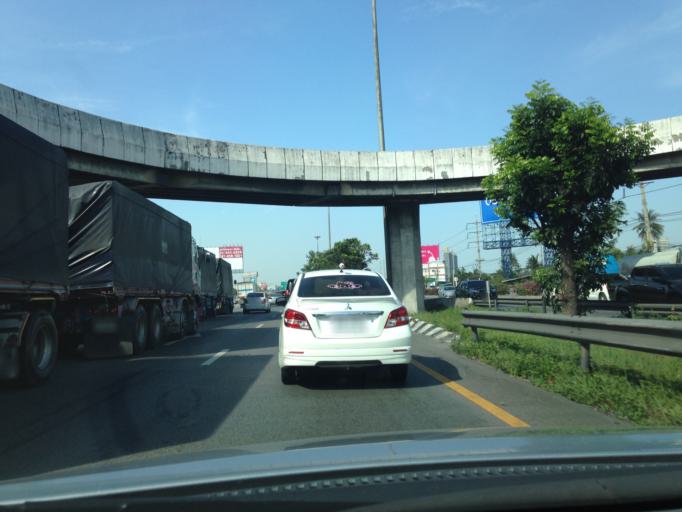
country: TH
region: Nonthaburi
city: Bang Yai
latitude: 13.8599
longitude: 100.4112
